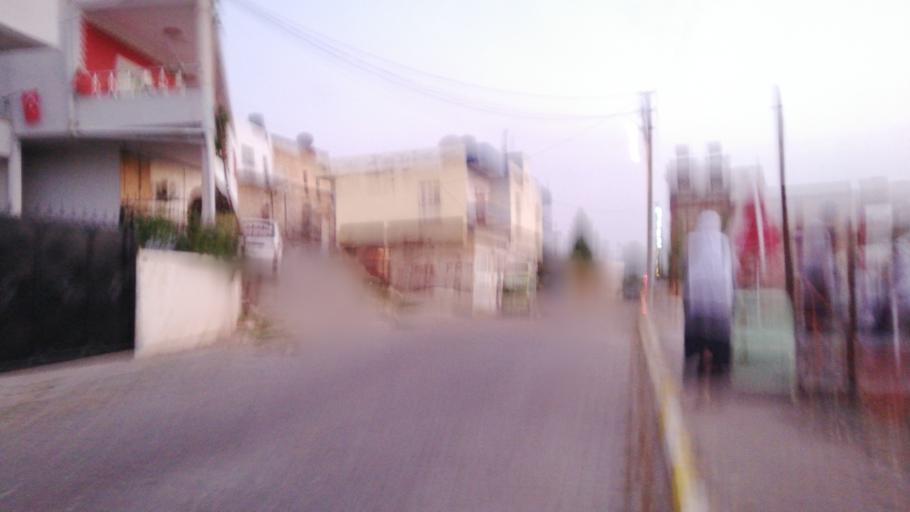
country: TR
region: Mardin
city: Kindirip
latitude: 37.4484
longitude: 41.2205
